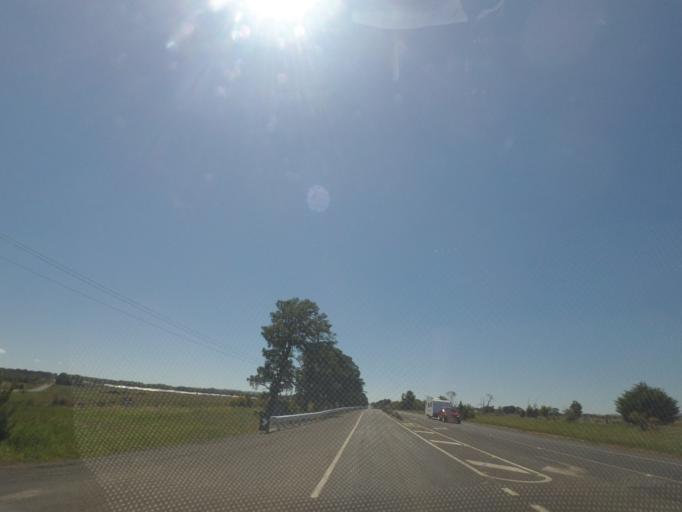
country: AU
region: Victoria
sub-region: Hume
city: Sunbury
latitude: -37.3721
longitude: 144.7455
